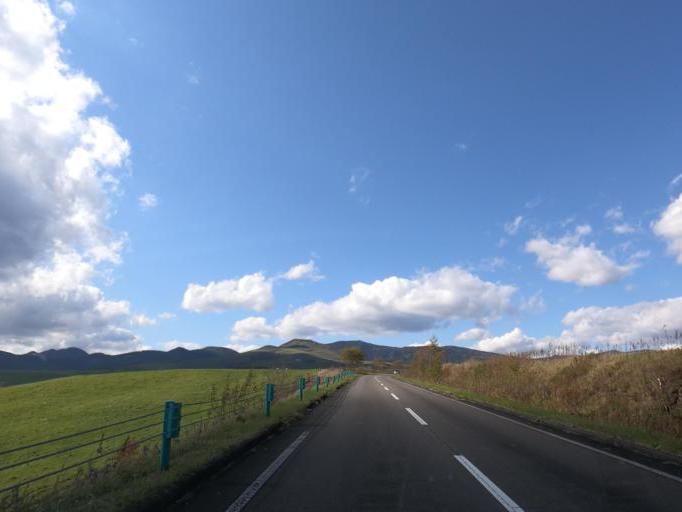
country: JP
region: Hokkaido
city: Otofuke
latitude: 43.2793
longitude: 143.2239
